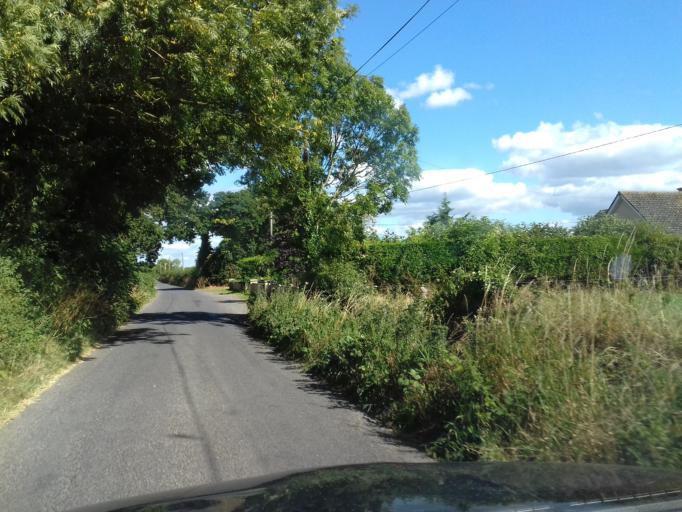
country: IE
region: Leinster
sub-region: Kilkenny
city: Callan
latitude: 52.5346
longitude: -7.3416
